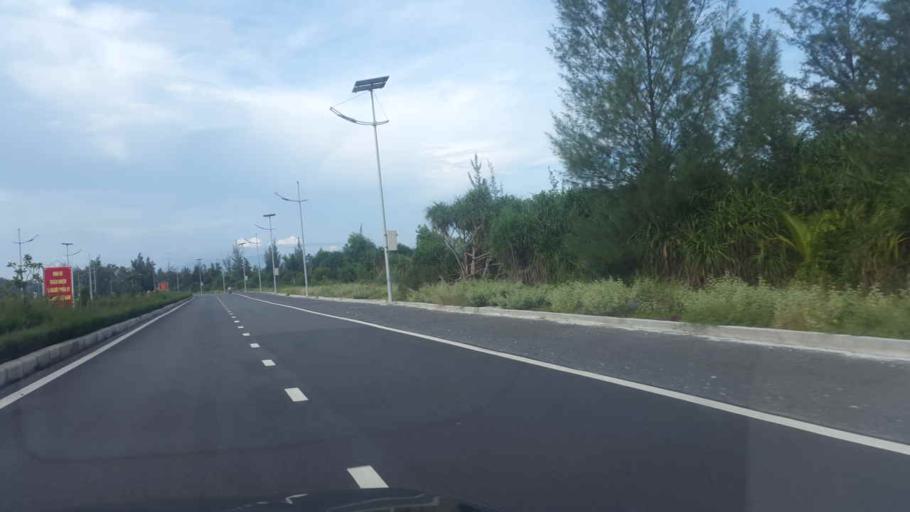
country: VN
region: Khanh Hoa
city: Cam Ranh
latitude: 11.9357
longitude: 109.2156
